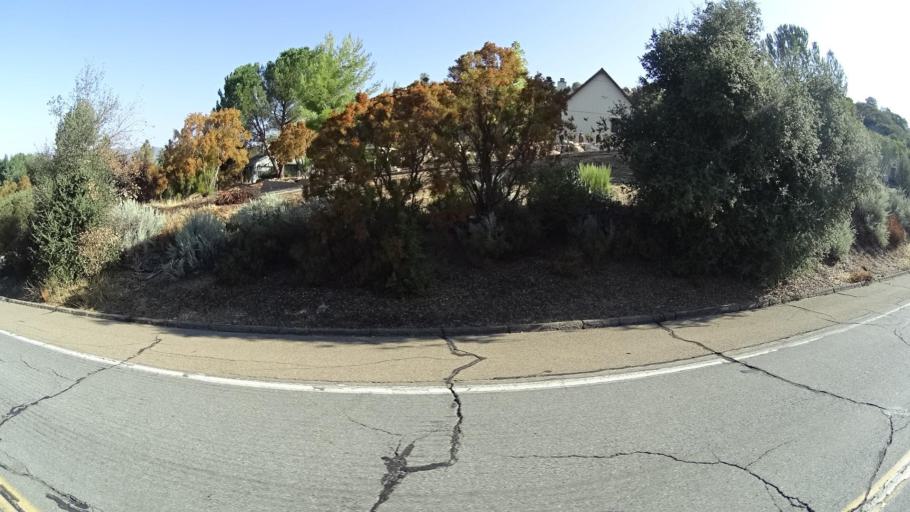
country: US
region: California
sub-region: San Diego County
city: Pine Valley
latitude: 32.8185
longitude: -116.5242
